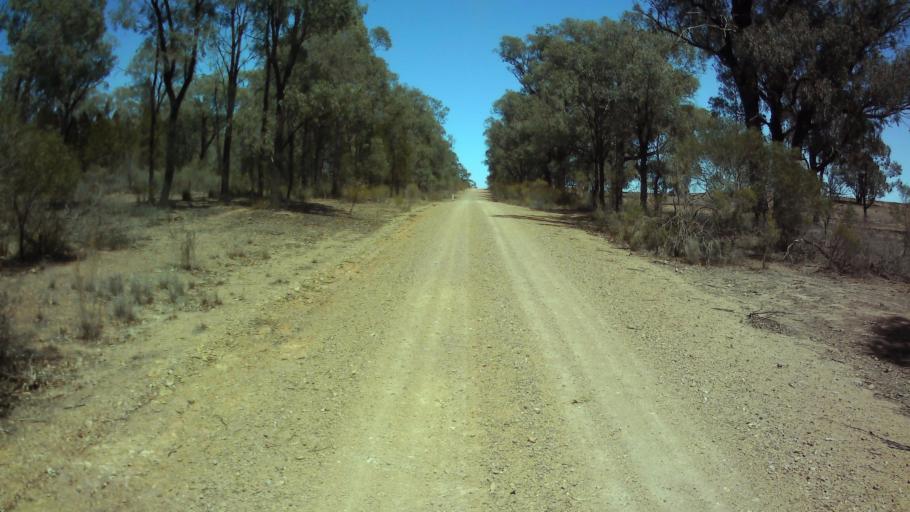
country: AU
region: New South Wales
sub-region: Forbes
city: Forbes
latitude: -33.6956
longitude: 147.8389
